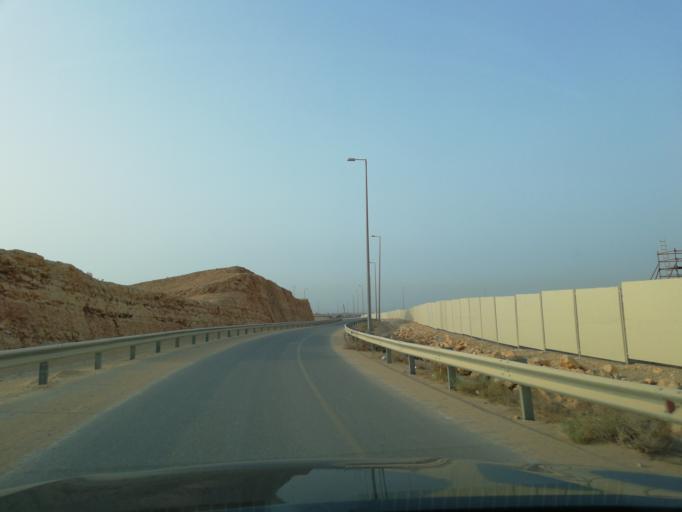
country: OM
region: Muhafazat Masqat
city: Bawshar
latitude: 23.5491
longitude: 58.2935
